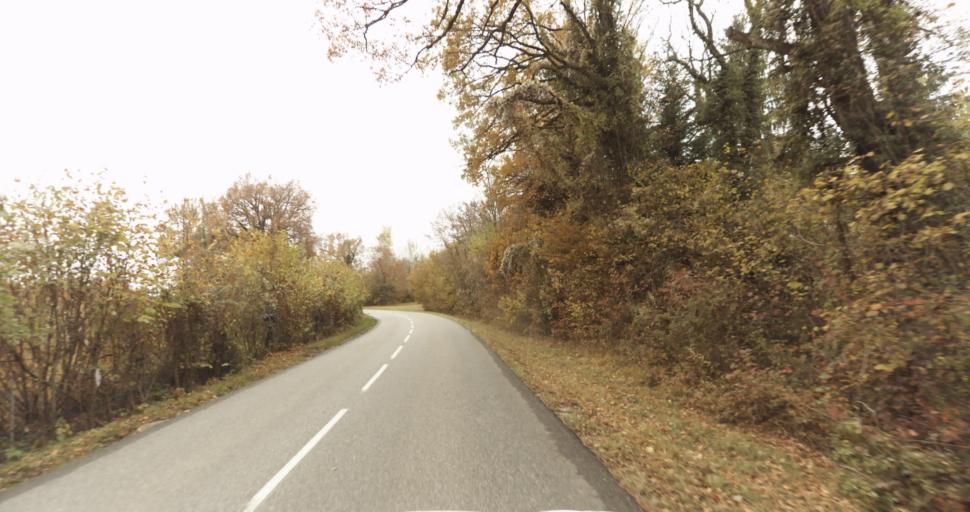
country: FR
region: Rhone-Alpes
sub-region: Departement de la Haute-Savoie
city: Seynod
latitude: 45.8540
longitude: 6.0856
